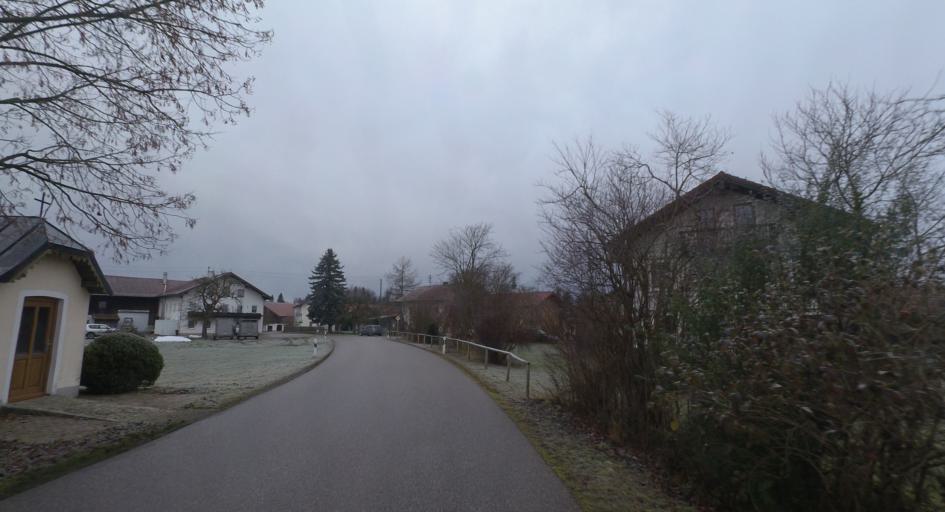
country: DE
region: Bavaria
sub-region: Upper Bavaria
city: Traunreut
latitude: 47.9383
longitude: 12.6086
